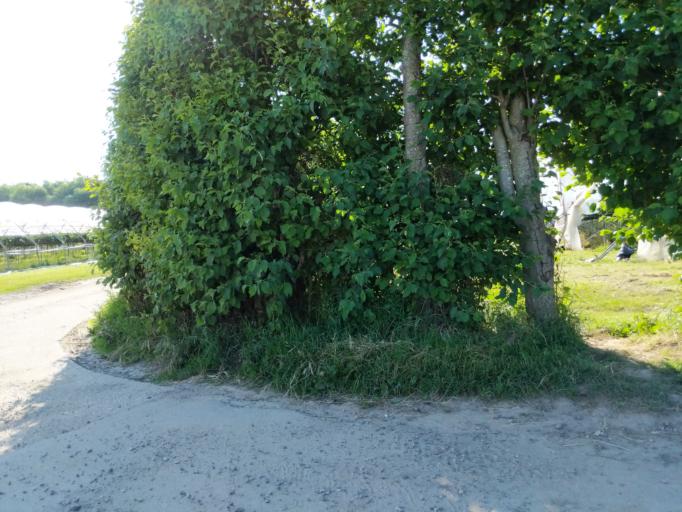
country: GB
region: England
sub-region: Kent
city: Faversham
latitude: 51.3301
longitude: 0.9281
